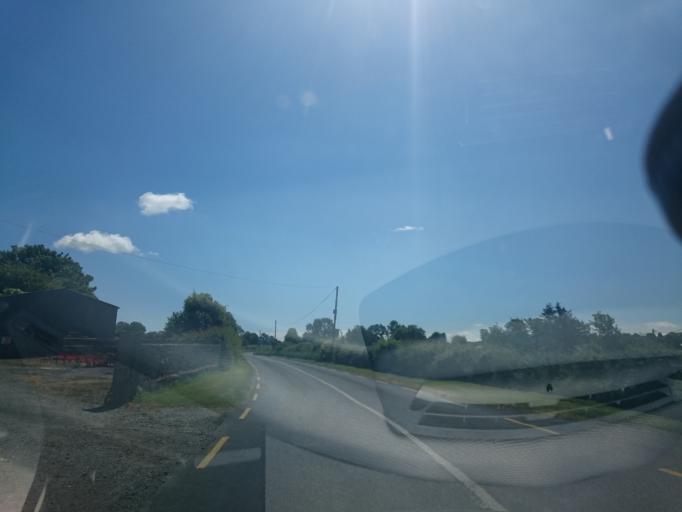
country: IE
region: Leinster
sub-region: Kilkenny
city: Graiguenamanagh
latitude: 52.5994
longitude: -6.9924
